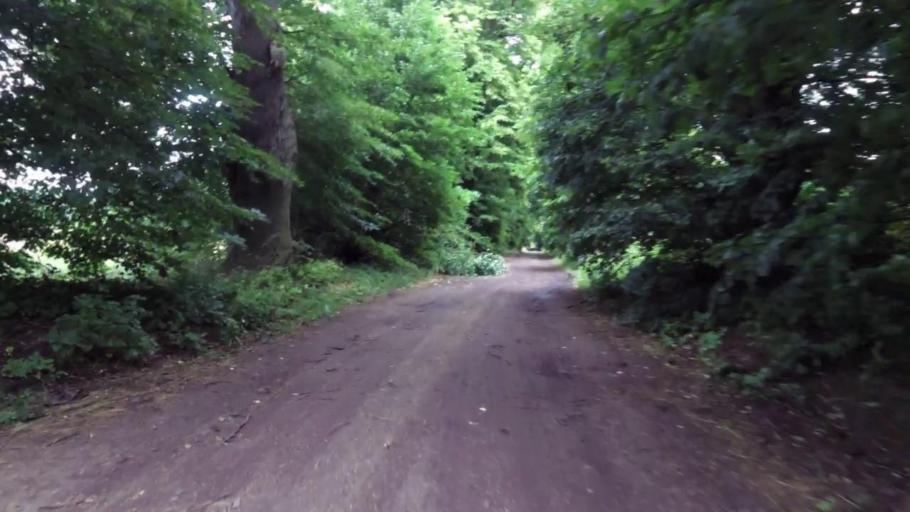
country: PL
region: West Pomeranian Voivodeship
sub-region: Powiat pyrzycki
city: Lipiany
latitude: 52.9705
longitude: 14.9281
